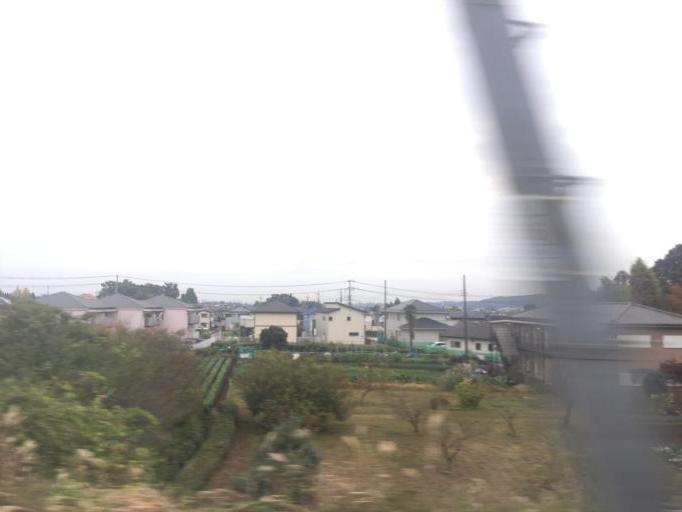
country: JP
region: Saitama
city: Hanno
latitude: 35.8411
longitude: 139.3341
